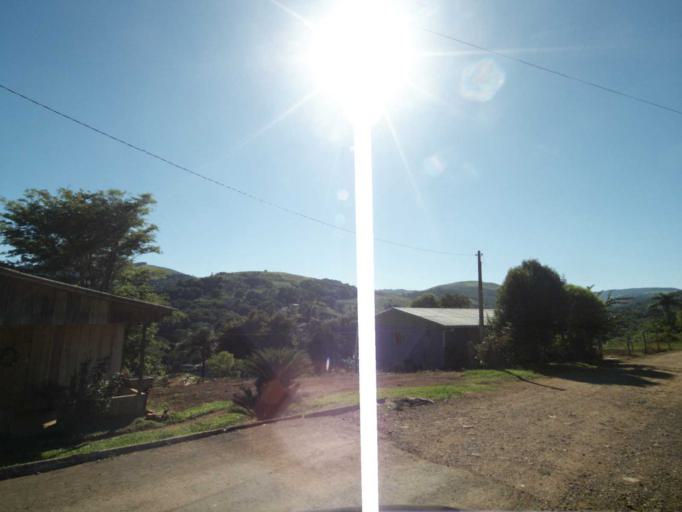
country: BR
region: Parana
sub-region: Francisco Beltrao
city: Francisco Beltrao
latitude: -26.1451
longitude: -53.3092
